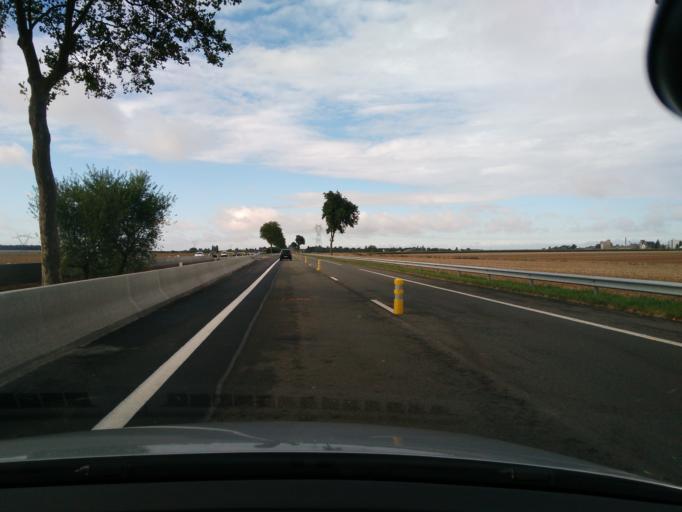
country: FR
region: Centre
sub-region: Departement d'Eure-et-Loir
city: Bu
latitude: 48.7688
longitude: 1.5352
